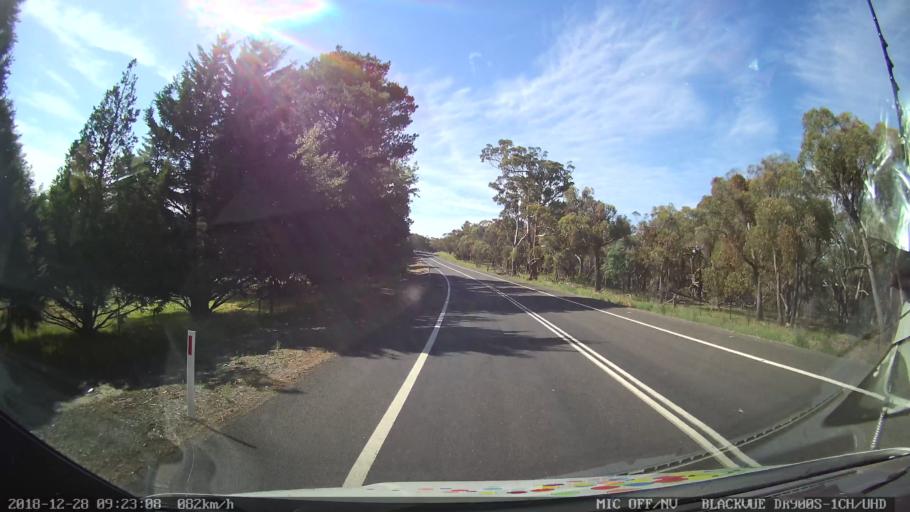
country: AU
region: New South Wales
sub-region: Upper Lachlan Shire
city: Crookwell
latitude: -34.3820
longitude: 149.3833
